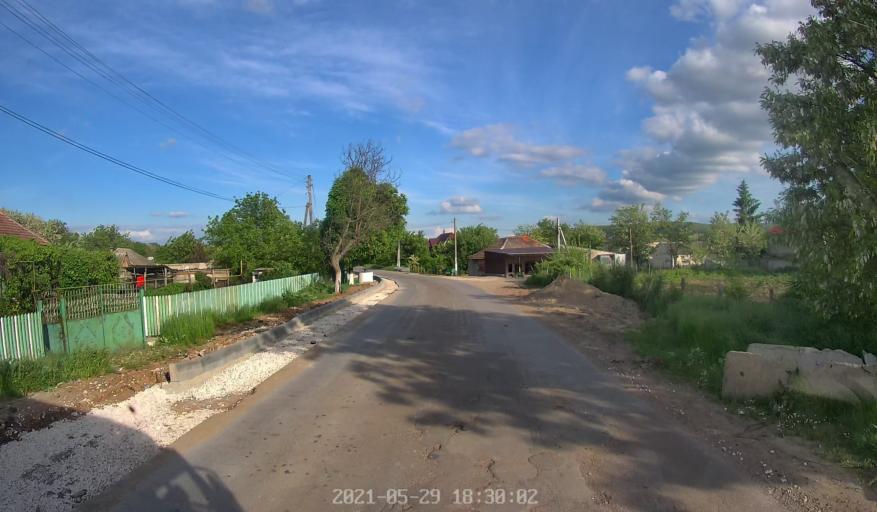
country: MD
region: Chisinau
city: Singera
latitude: 46.8242
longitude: 28.8757
